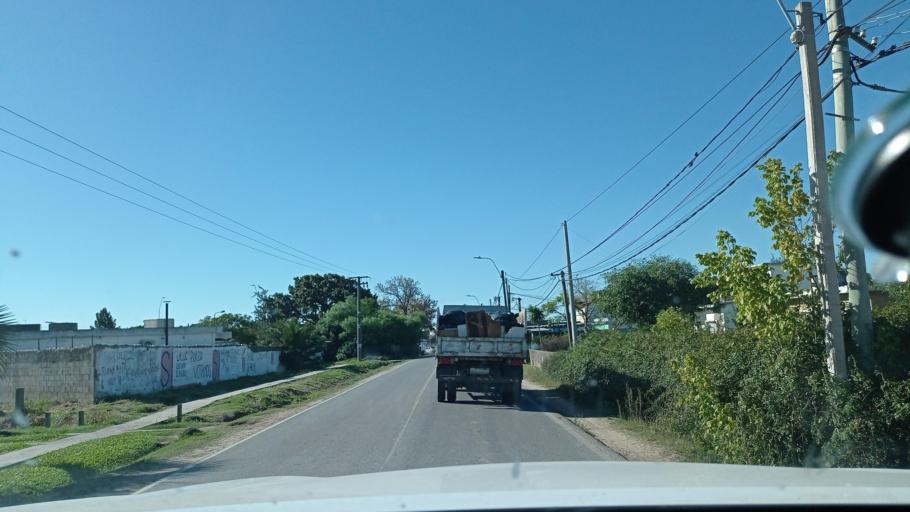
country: UY
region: Canelones
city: Joaquin Suarez
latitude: -34.7535
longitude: -56.0009
